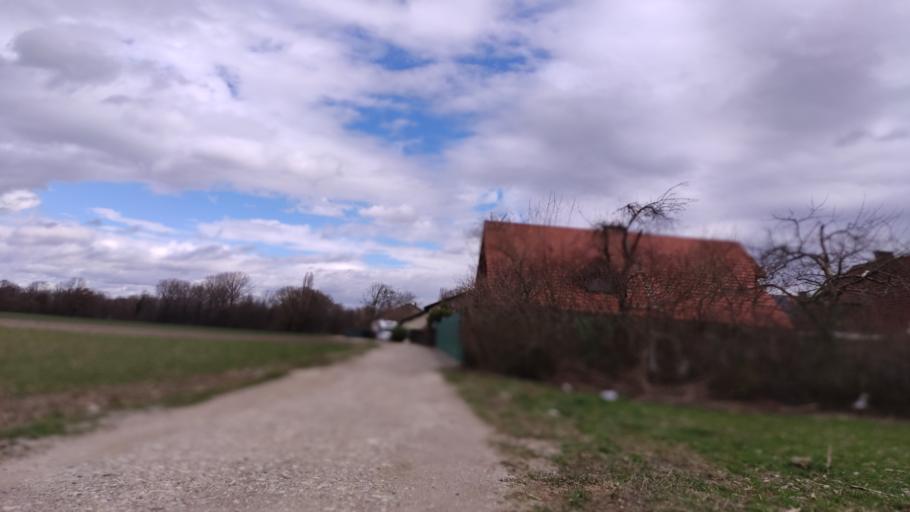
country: DE
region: Bavaria
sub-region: Upper Bavaria
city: Emmering
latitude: 48.1817
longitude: 11.2936
